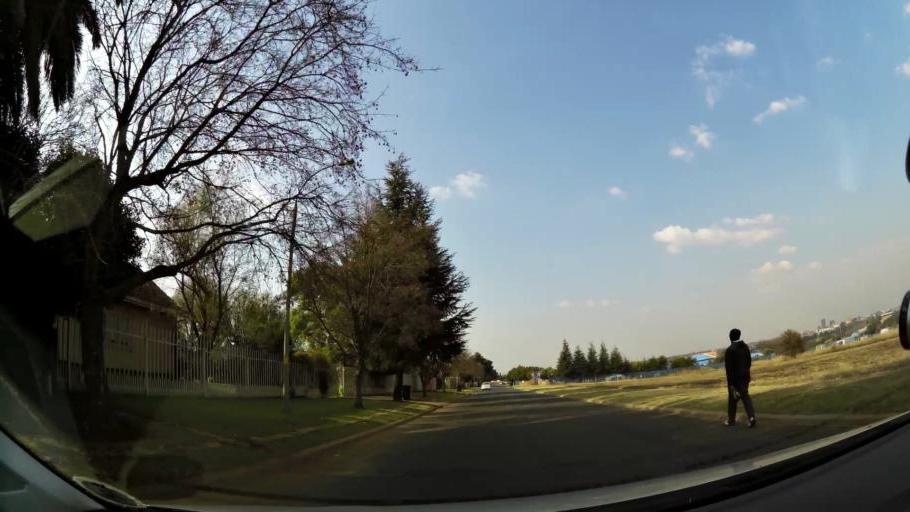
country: ZA
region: Gauteng
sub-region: City of Johannesburg Metropolitan Municipality
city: Modderfontein
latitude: -26.1003
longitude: 28.1996
